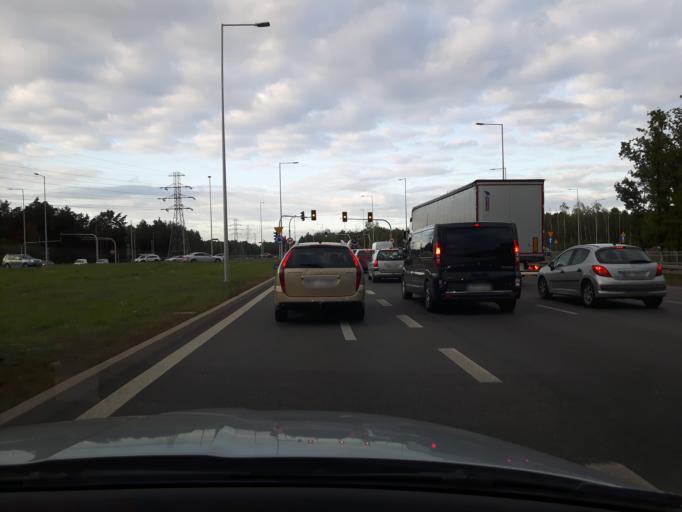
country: PL
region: Masovian Voivodeship
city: Zielonka
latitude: 52.2936
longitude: 21.1389
